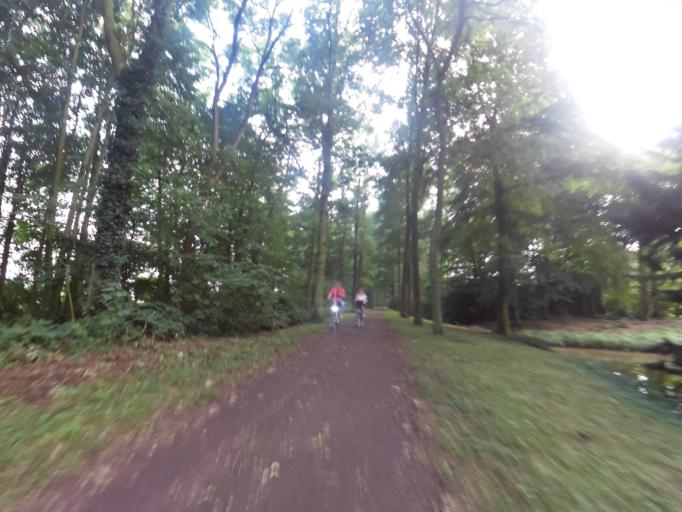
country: NL
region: Gelderland
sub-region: Oude IJsselstreek
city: Gendringen
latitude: 51.8521
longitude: 6.4083
